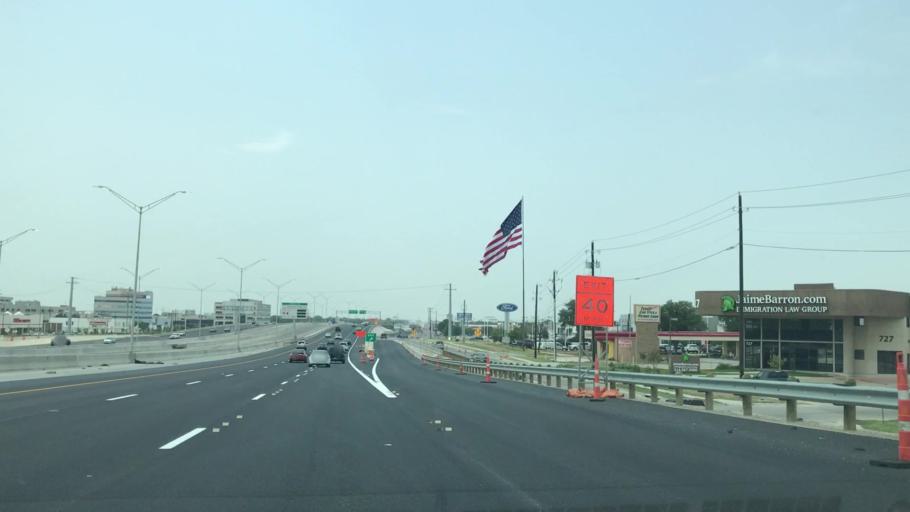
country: US
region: Texas
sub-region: Dallas County
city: Irving
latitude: 32.8374
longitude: -96.9532
